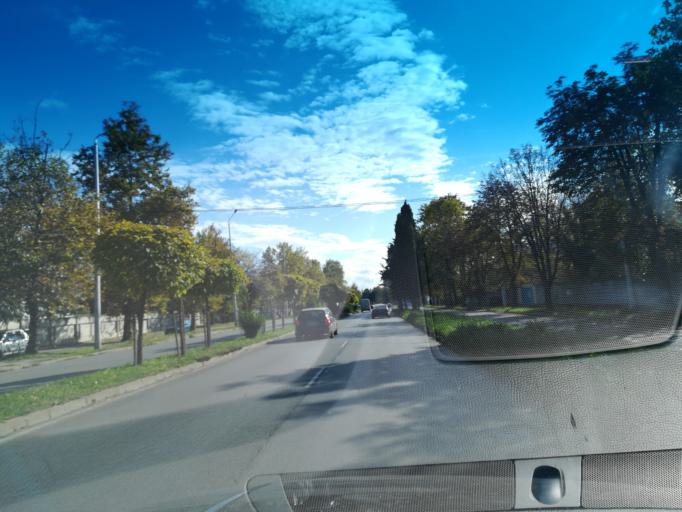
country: BG
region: Stara Zagora
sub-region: Obshtina Stara Zagora
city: Stara Zagora
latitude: 42.4115
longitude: 25.6392
